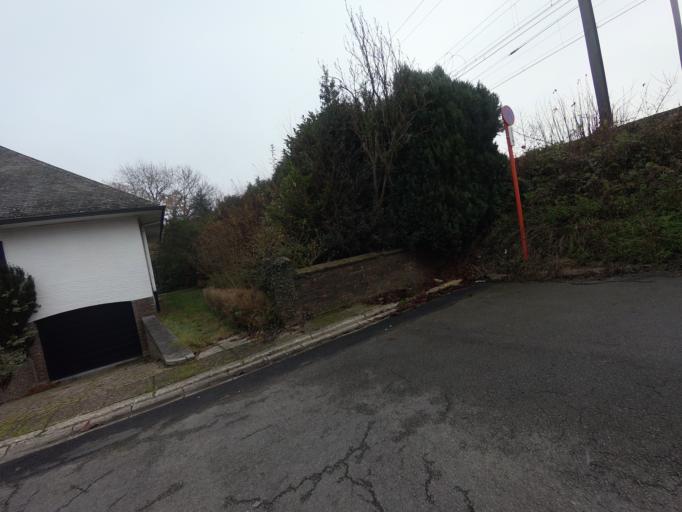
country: BE
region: Flanders
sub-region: Provincie Oost-Vlaanderen
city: Ninove
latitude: 50.8382
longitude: 4.0183
